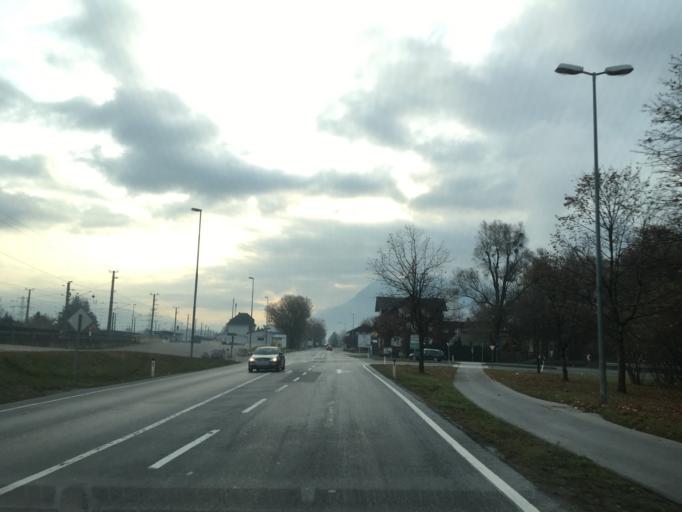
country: AT
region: Vorarlberg
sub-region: Politischer Bezirk Feldkirch
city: Gofis
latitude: 47.2210
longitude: 9.6356
